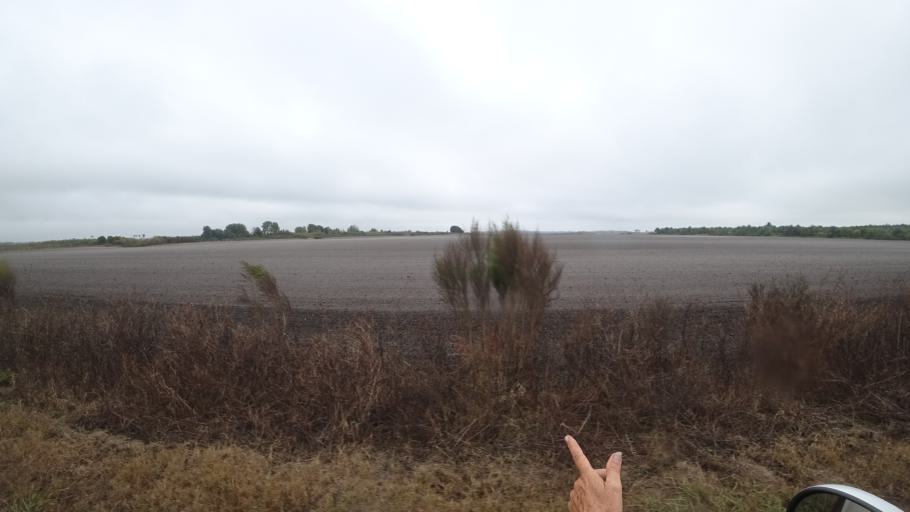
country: US
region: Florida
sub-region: Sarasota County
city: Warm Mineral Springs
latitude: 27.2814
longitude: -82.1775
